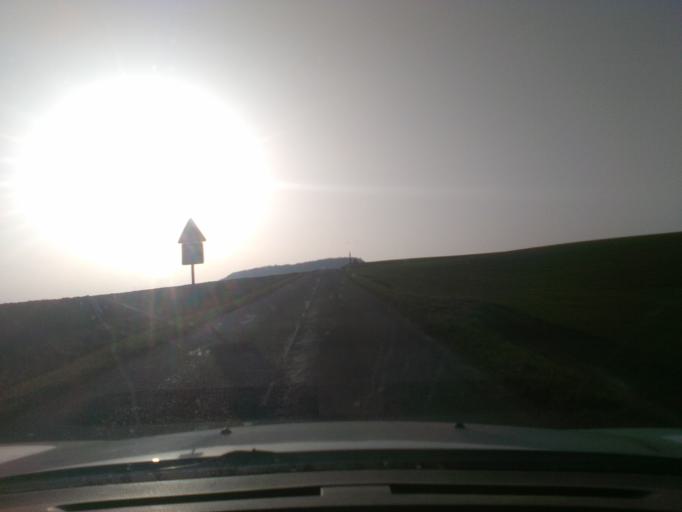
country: FR
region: Lorraine
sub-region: Departement des Vosges
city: Vittel
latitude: 48.2728
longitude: 6.0214
